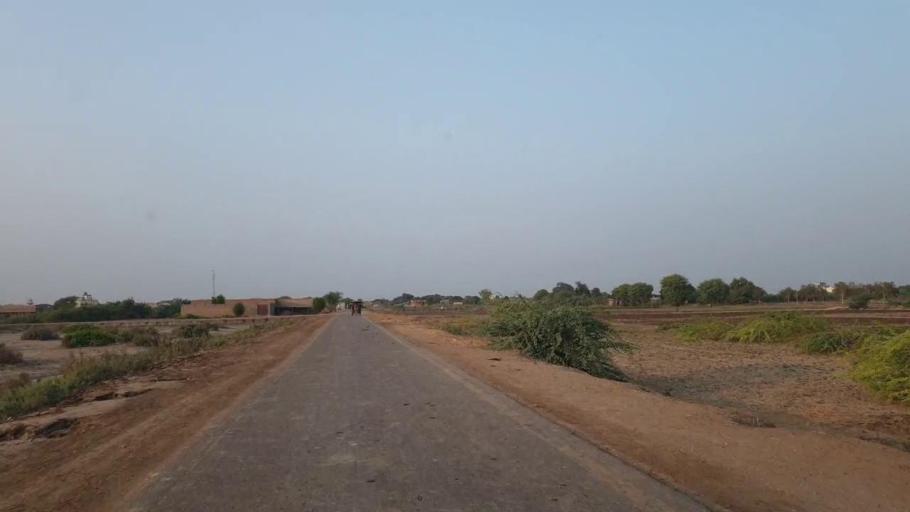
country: PK
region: Sindh
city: Tando Ghulam Ali
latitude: 25.1398
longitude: 68.9587
